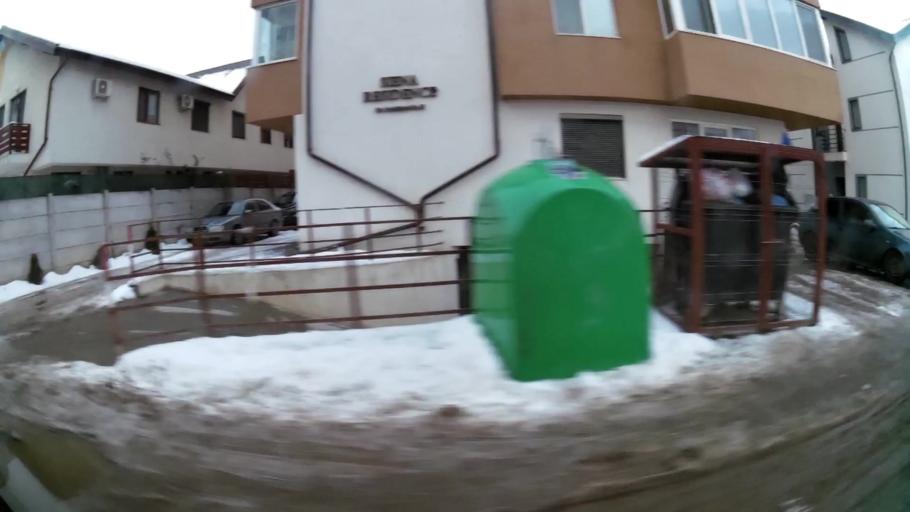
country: RO
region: Ilfov
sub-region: Comuna Popesti-Leordeni
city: Popesti-Leordeni
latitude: 44.3711
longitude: 26.1567
